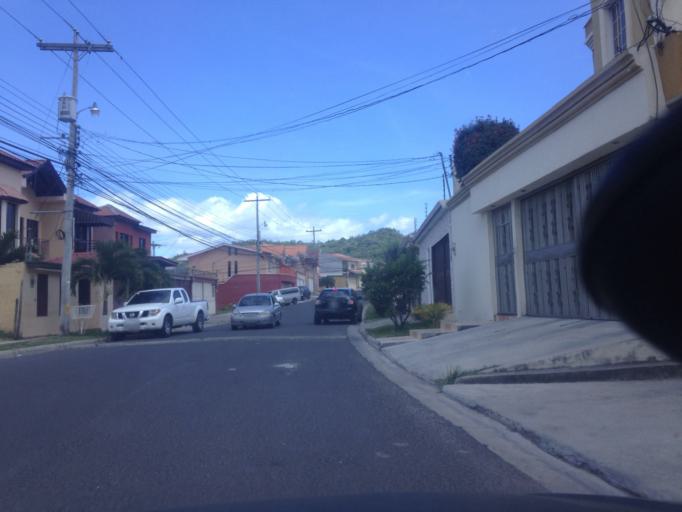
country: HN
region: Francisco Morazan
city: Yaguacire
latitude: 14.0437
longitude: -87.2321
